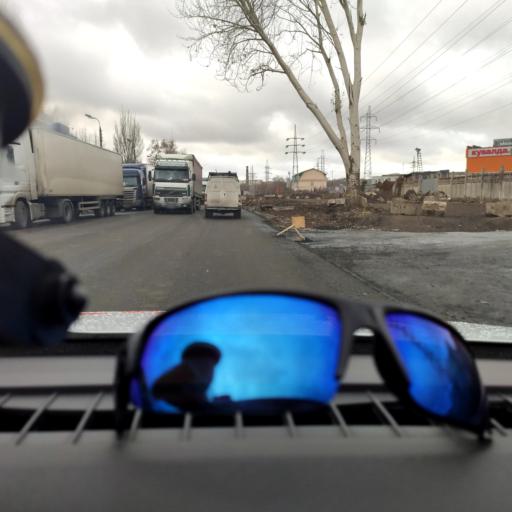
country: RU
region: Samara
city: Samara
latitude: 53.1943
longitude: 50.2392
